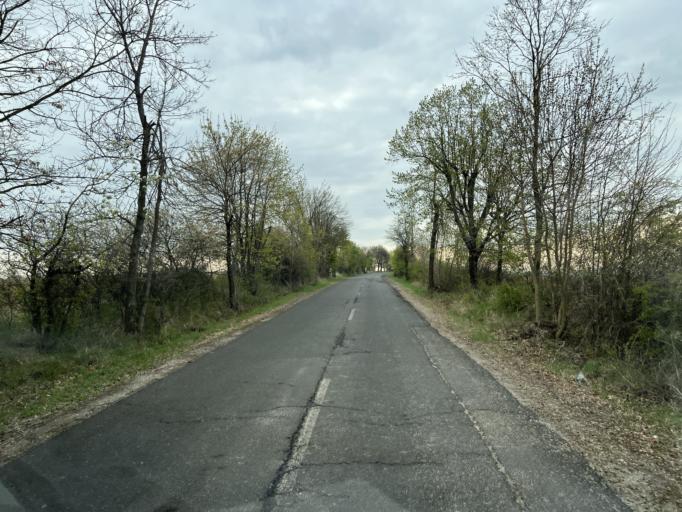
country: HU
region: Pest
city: Acsa
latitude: 47.7896
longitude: 19.4084
